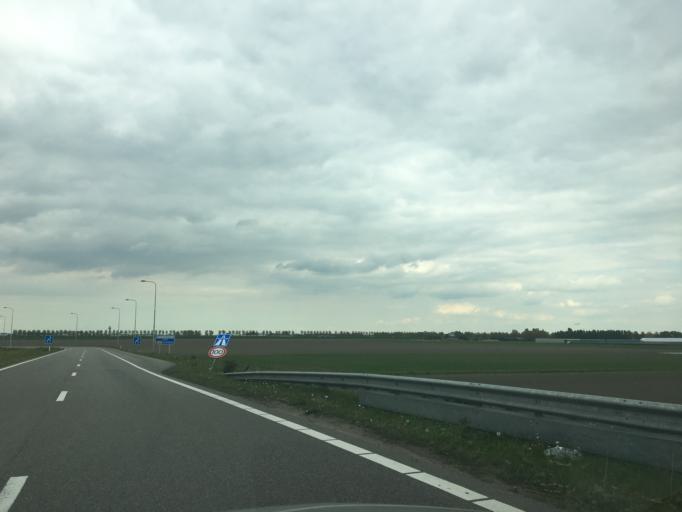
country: NL
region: North Holland
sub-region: Gemeente Haarlemmermeer
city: Hoofddorp
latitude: 52.2708
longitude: 4.7065
